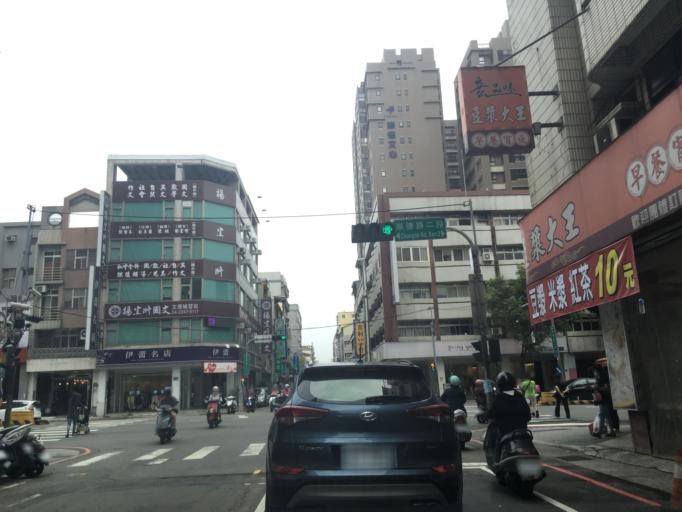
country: TW
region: Taiwan
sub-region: Taichung City
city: Taichung
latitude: 24.1734
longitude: 120.6852
